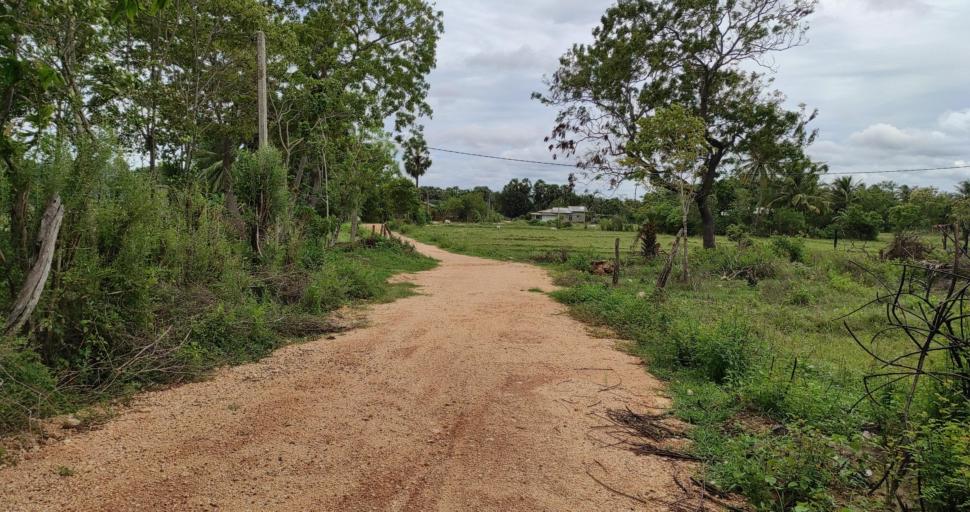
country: LK
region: Eastern Province
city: Trincomalee
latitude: 8.4461
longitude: 81.0512
